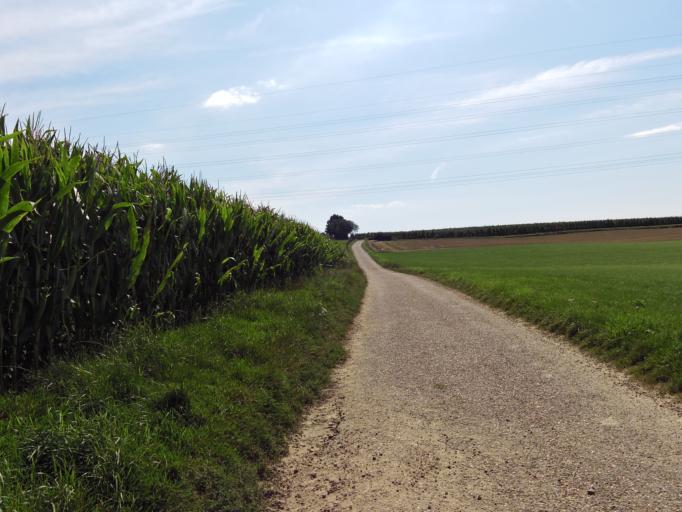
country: NL
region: Limburg
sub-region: Gemeente Voerendaal
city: Kunrade
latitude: 50.8574
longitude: 5.9108
